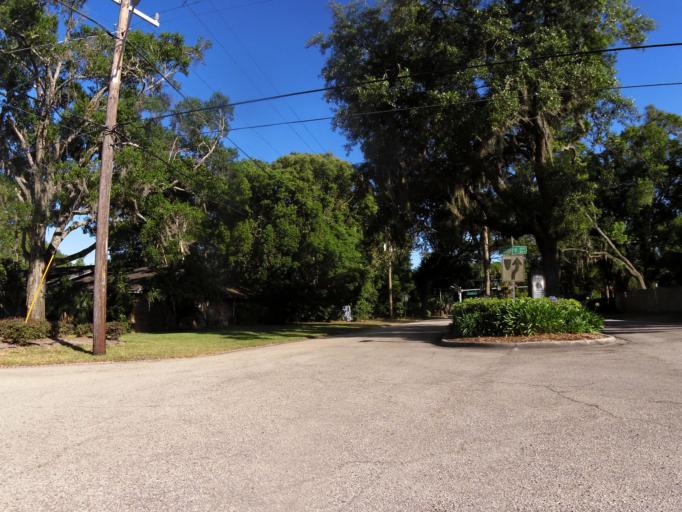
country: US
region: Florida
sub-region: Duval County
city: Jacksonville
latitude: 30.3104
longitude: -81.6144
